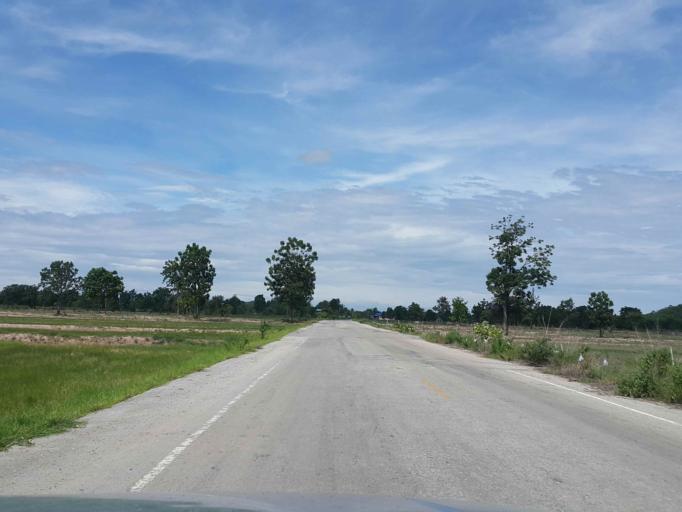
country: TH
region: Sukhothai
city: Ban Dan Lan Hoi
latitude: 17.1097
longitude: 99.4881
